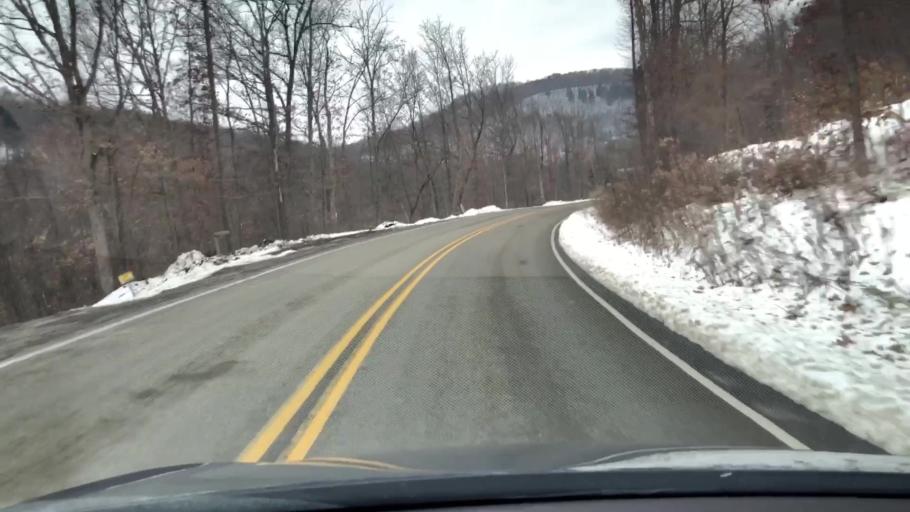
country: US
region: Pennsylvania
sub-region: Elk County
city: Saint Marys
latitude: 41.2767
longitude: -78.4654
